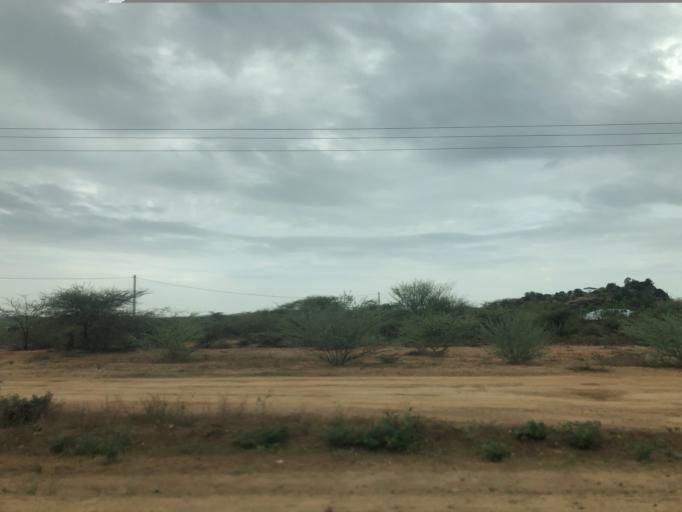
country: ET
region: Southern Nations, Nationalities, and People's Region
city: Turmi
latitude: 4.9750
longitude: 36.4846
